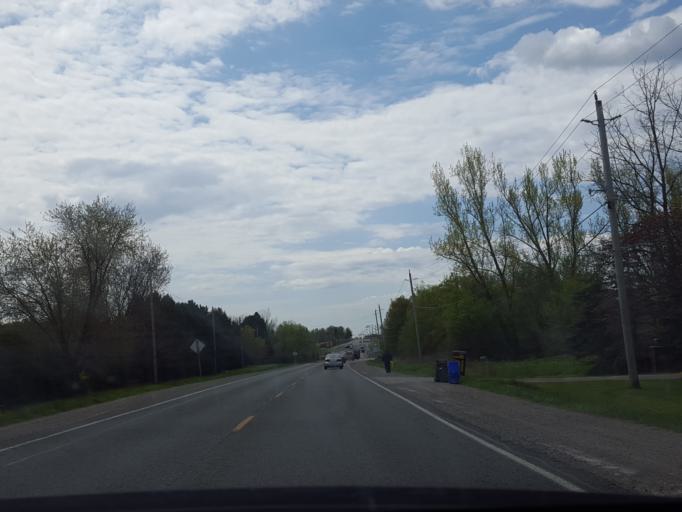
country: CA
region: Ontario
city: Oshawa
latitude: 43.9165
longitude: -78.7041
